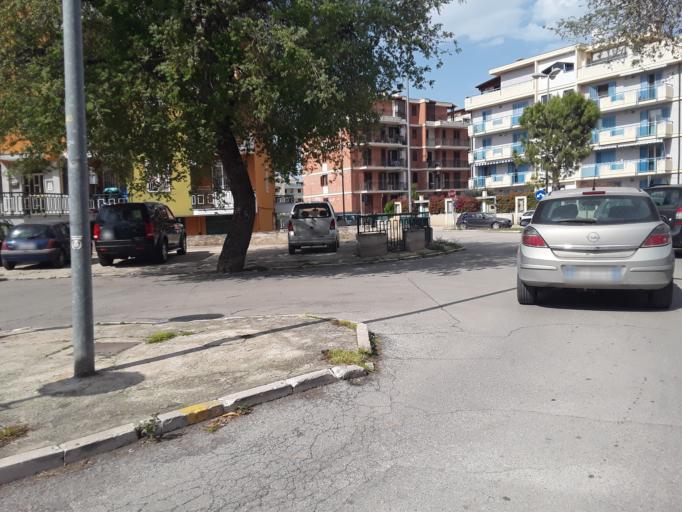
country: IT
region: Apulia
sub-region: Provincia di Bari
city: Ruvo di Puglia
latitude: 41.1220
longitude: 16.4774
